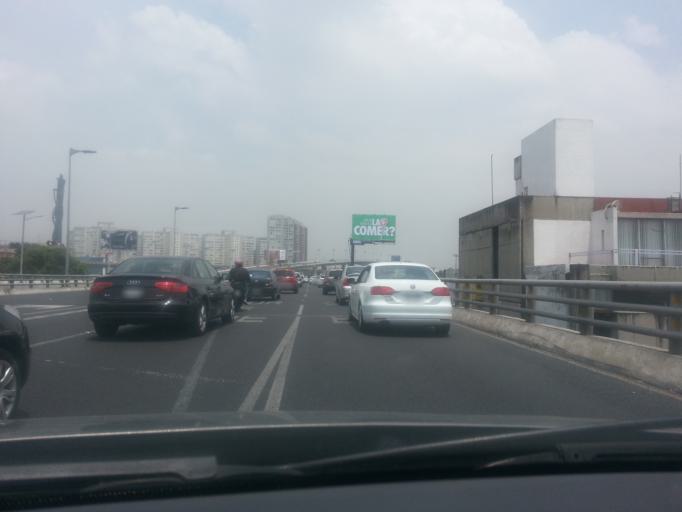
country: MX
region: Mexico City
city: Alvaro Obregon
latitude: 19.3806
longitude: -99.1916
